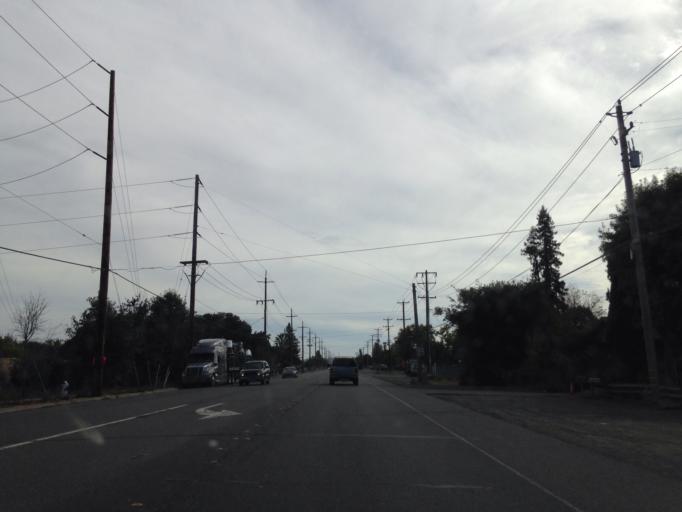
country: US
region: California
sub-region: Sonoma County
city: Rohnert Park
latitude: 38.3793
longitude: -122.7136
